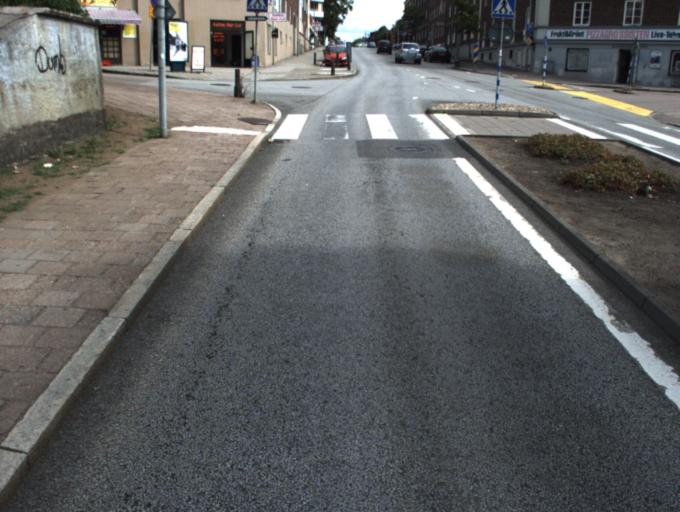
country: SE
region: Skane
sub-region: Helsingborg
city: Helsingborg
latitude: 56.0386
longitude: 12.7096
